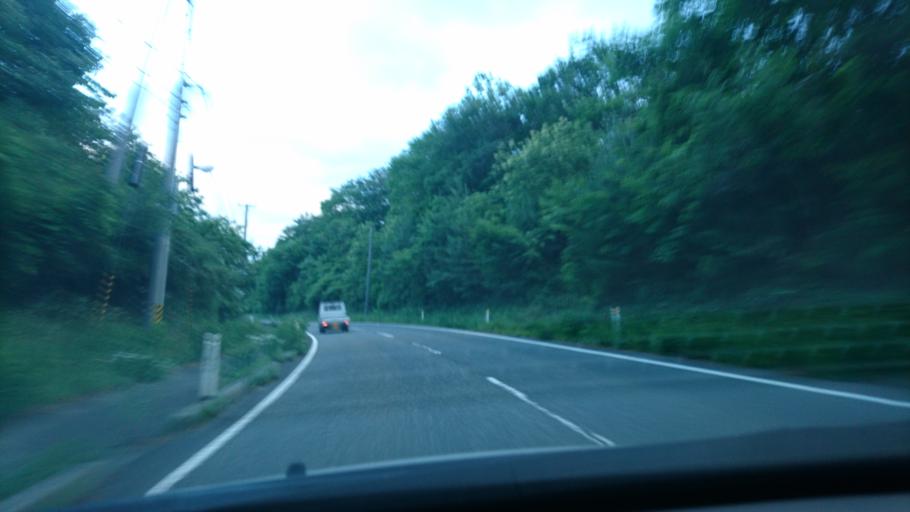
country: JP
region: Iwate
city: Ichinoseki
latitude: 38.7851
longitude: 141.0559
